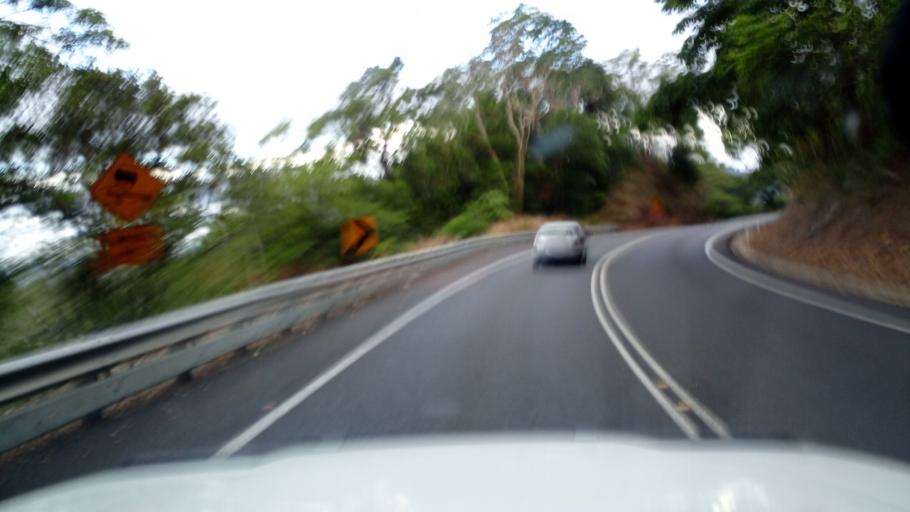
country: AU
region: Queensland
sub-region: Cairns
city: Redlynch
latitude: -16.8505
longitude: 145.6861
